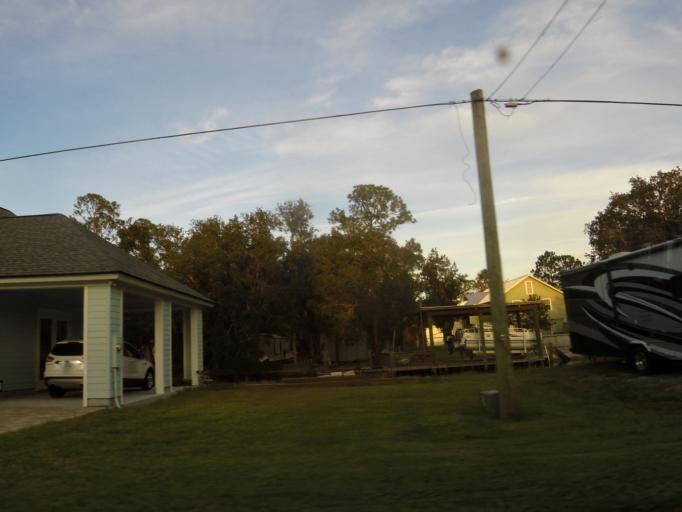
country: US
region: Florida
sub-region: Saint Johns County
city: Palm Valley
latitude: 30.1319
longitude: -81.3838
